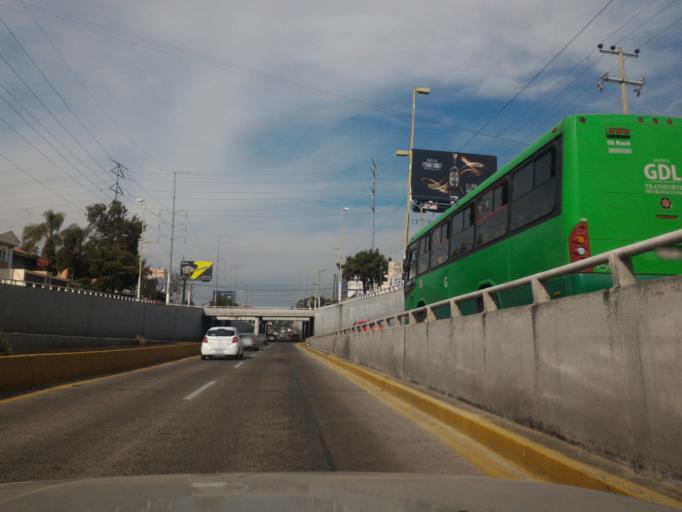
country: MX
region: Jalisco
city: Guadalajara
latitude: 20.6812
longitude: -103.4211
